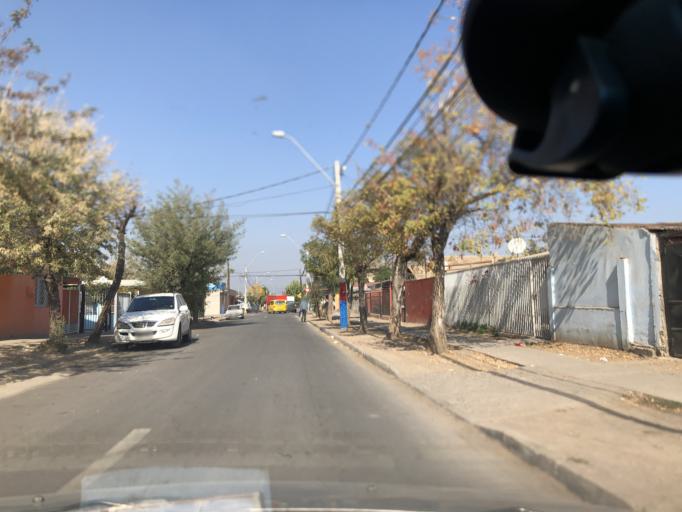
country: CL
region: Santiago Metropolitan
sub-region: Provincia de Cordillera
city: Puente Alto
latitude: -33.6174
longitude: -70.5814
